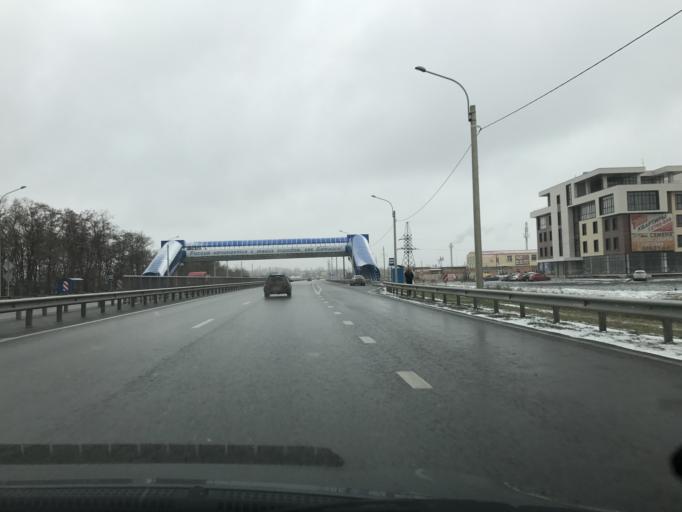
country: RU
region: Rostov
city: Bataysk
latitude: 47.1401
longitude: 39.7761
